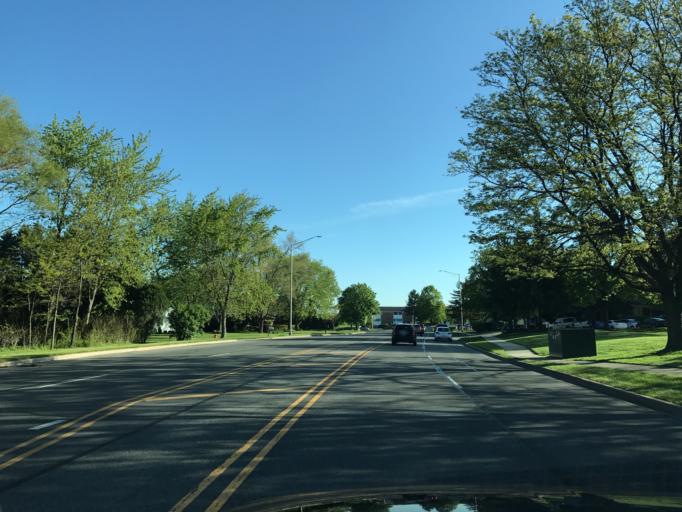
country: US
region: Illinois
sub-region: DuPage County
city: Naperville
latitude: 41.7739
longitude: -88.1098
